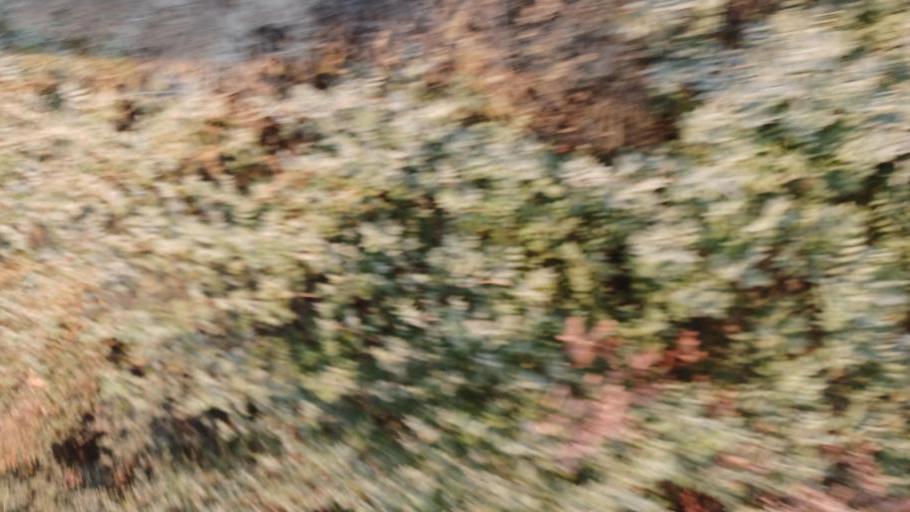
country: CY
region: Limassol
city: Pissouri
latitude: 34.7021
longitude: 32.6666
